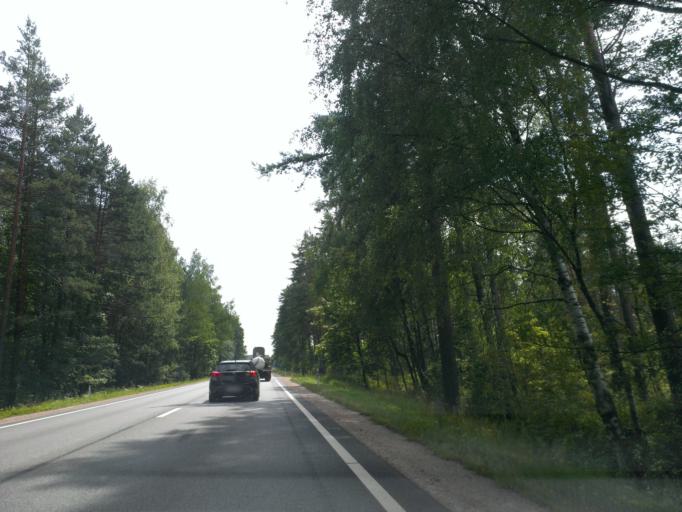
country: LV
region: Salaspils
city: Salaspils
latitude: 56.9476
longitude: 24.3799
